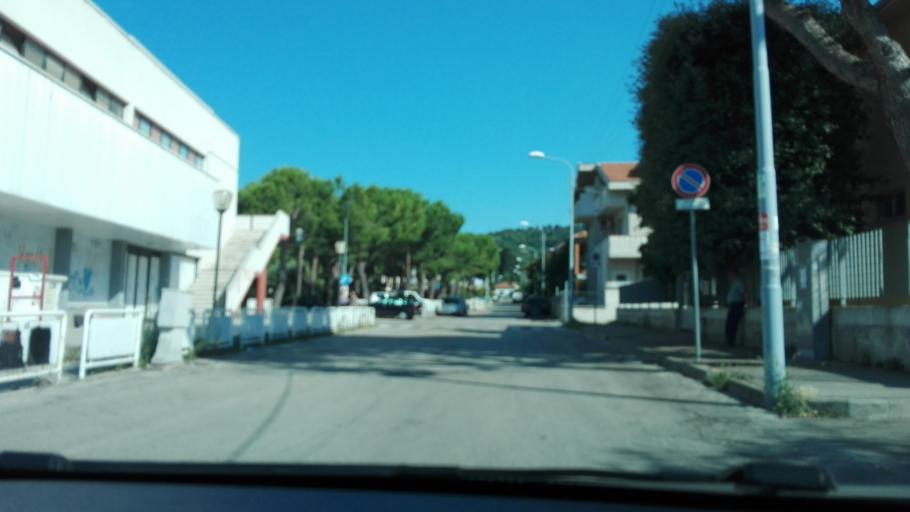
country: IT
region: Abruzzo
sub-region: Provincia di Pescara
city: Montesilvano Marina
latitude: 42.5036
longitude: 14.1361
